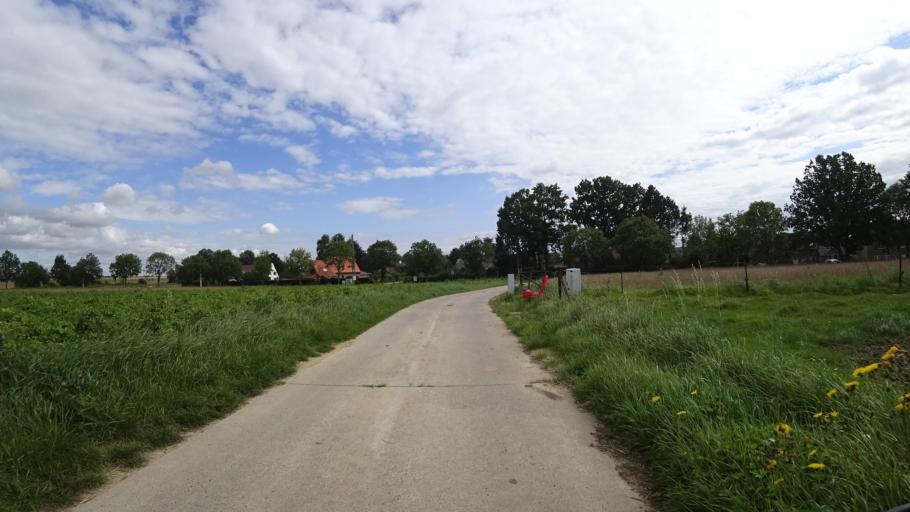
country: BE
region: Wallonia
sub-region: Province du Brabant Wallon
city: Walhain-Saint-Paul
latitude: 50.6501
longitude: 4.6601
